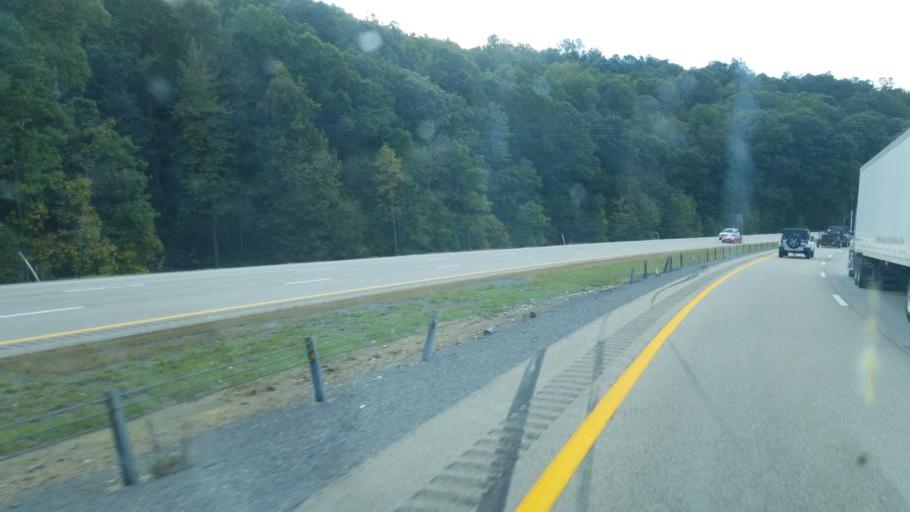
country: US
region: West Virginia
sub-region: Monongalia County
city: Cheat Lake
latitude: 39.6587
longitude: -79.8109
